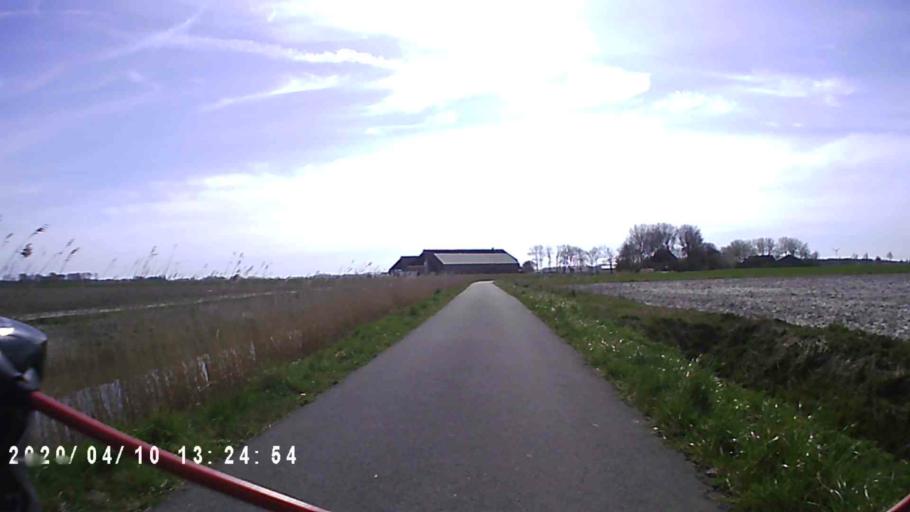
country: NL
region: Groningen
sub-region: Gemeente Zuidhorn
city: Oldehove
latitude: 53.3837
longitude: 6.4239
